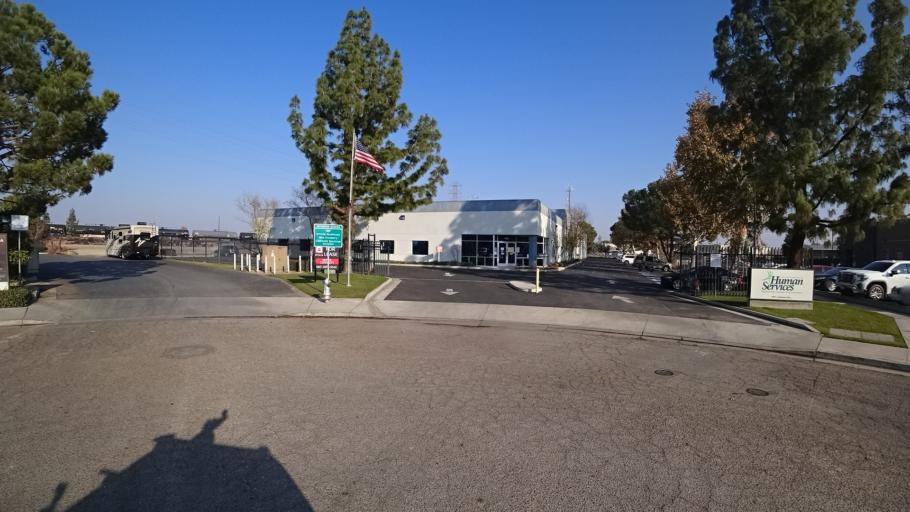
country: US
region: California
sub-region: Kern County
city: Bakersfield
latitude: 35.3703
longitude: -119.0555
